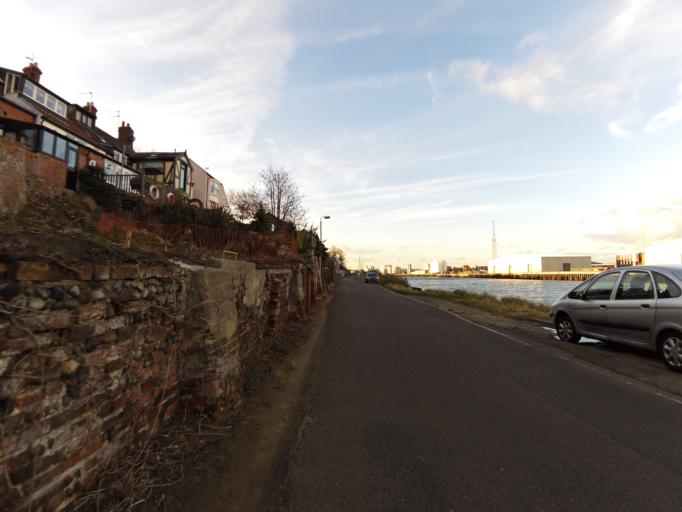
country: GB
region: England
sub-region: Norfolk
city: Gorleston-on-Sea
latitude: 52.5854
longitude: 1.7286
